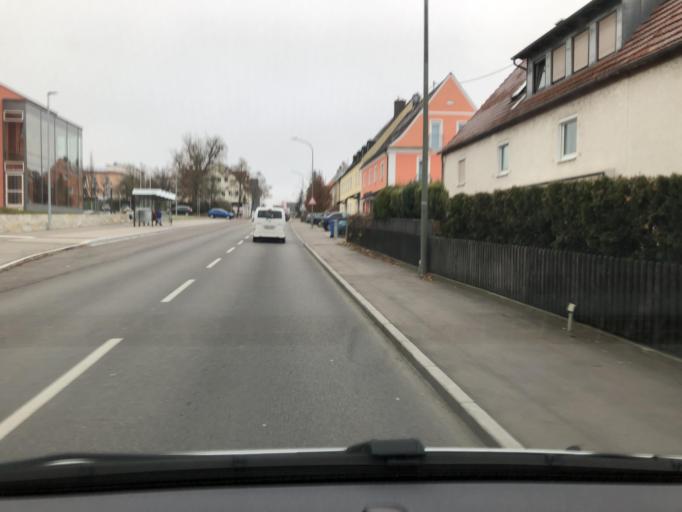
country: DE
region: Bavaria
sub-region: Swabia
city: Donauwoerth
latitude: 48.7265
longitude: 10.7783
